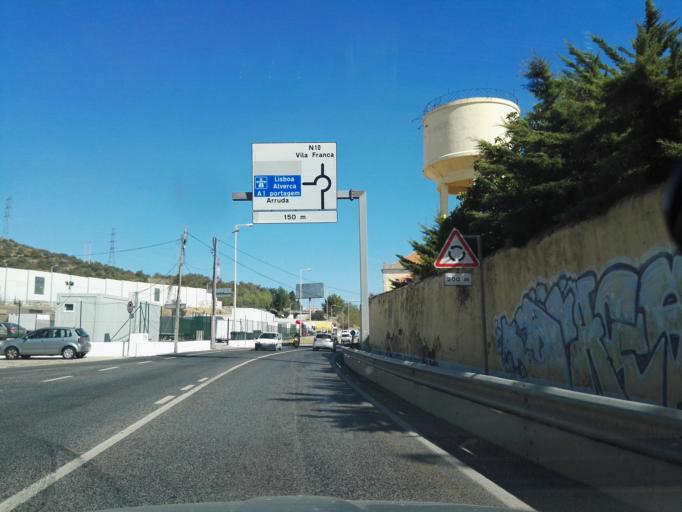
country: PT
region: Lisbon
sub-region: Vila Franca de Xira
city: Vila Franca de Xira
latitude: 38.9433
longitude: -8.9969
